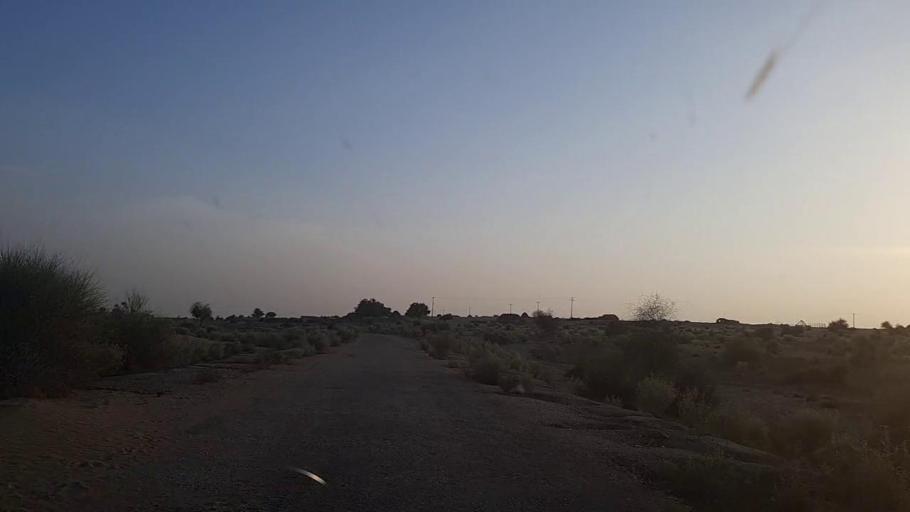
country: PK
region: Sindh
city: Khanpur
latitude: 27.5989
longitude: 69.4280
